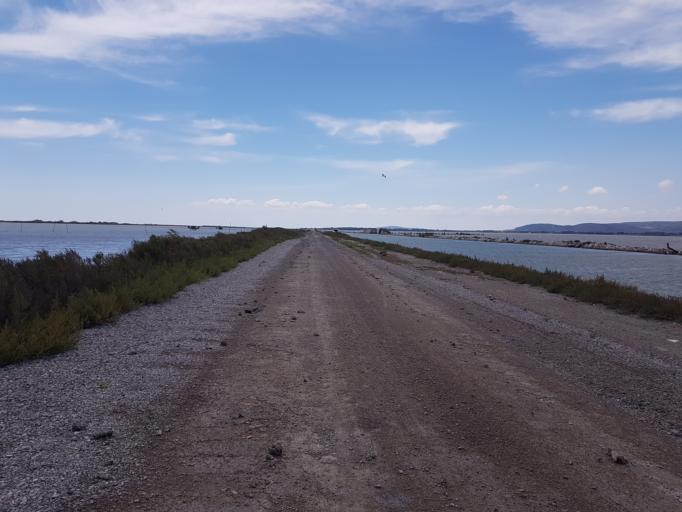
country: FR
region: Languedoc-Roussillon
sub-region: Departement de l'Herault
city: Villeneuve-les-Maguelone
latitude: 43.4939
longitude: 3.8505
